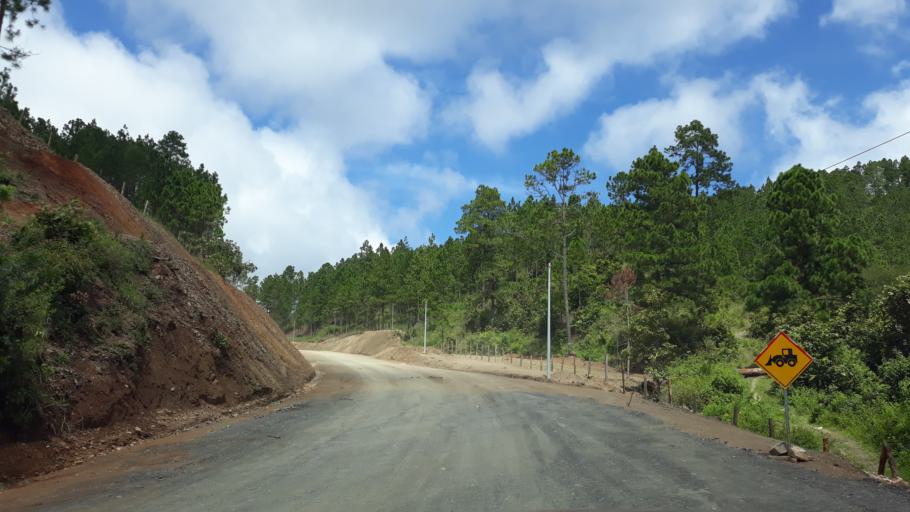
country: HN
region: El Paraiso
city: Santa Cruz
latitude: 13.7670
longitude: -86.6383
